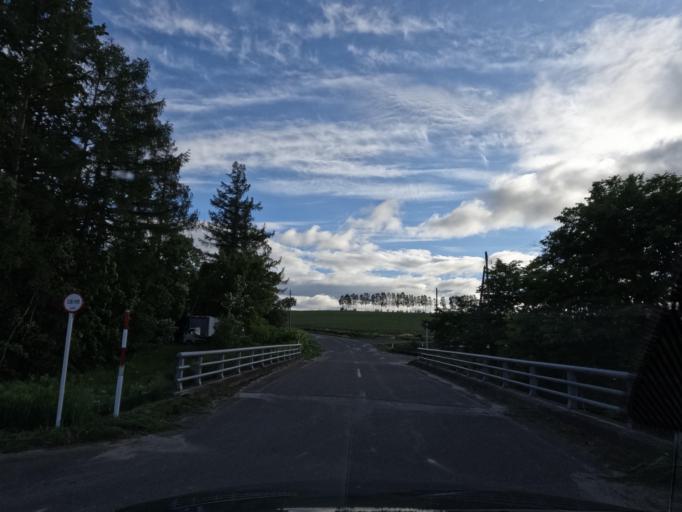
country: JP
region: Hokkaido
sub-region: Asahikawa-shi
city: Asahikawa
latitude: 43.6318
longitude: 142.4344
